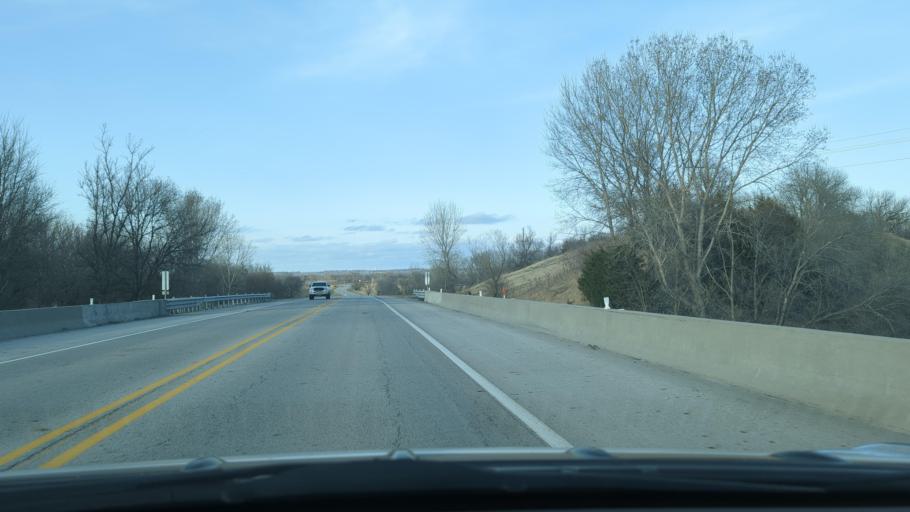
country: US
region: Nebraska
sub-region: Saunders County
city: Ashland
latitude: 41.0492
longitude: -96.3415
